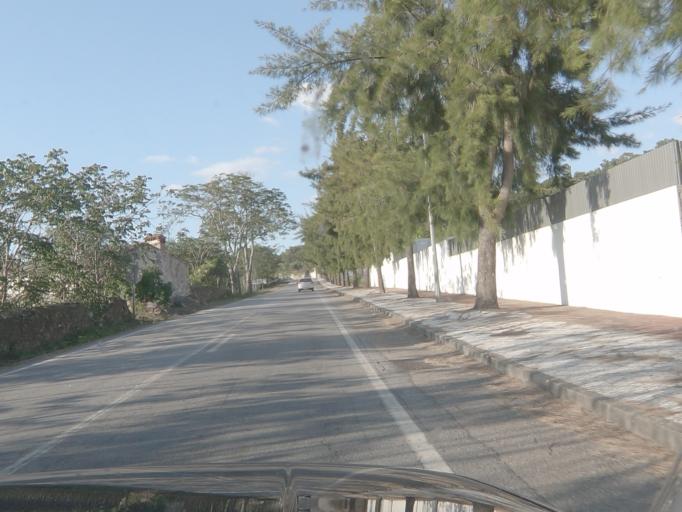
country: PT
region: Portalegre
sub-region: Portalegre
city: Portalegre
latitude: 39.3139
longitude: -7.4410
